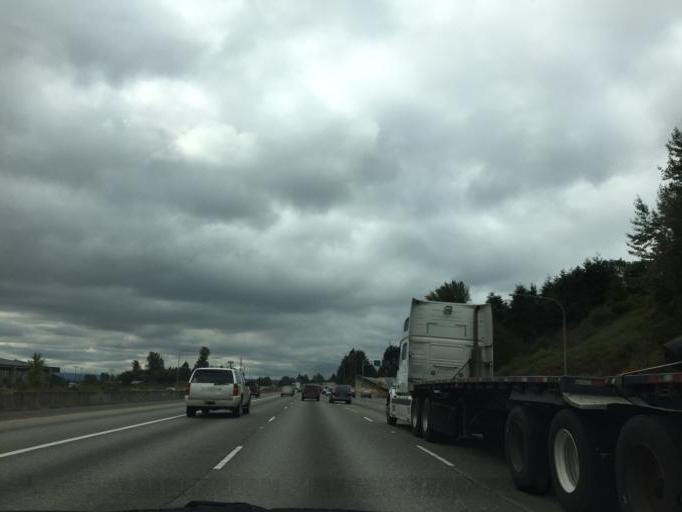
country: US
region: Washington
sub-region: King County
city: SeaTac
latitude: 47.4375
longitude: -122.2696
